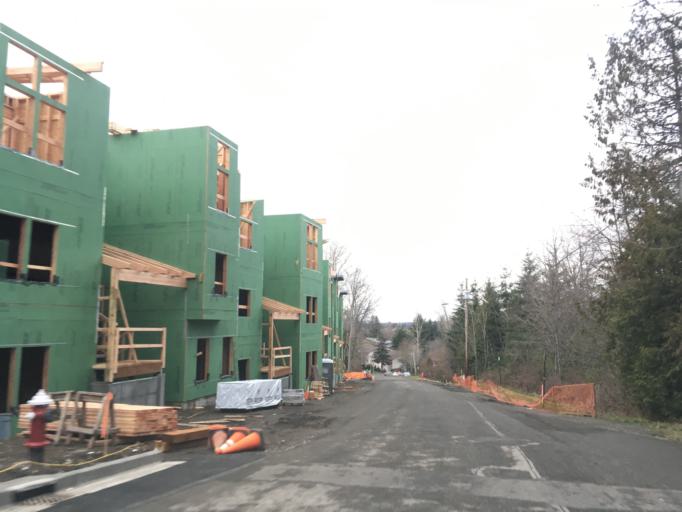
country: US
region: Washington
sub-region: Whatcom County
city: Bellingham
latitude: 48.7341
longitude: -122.4638
